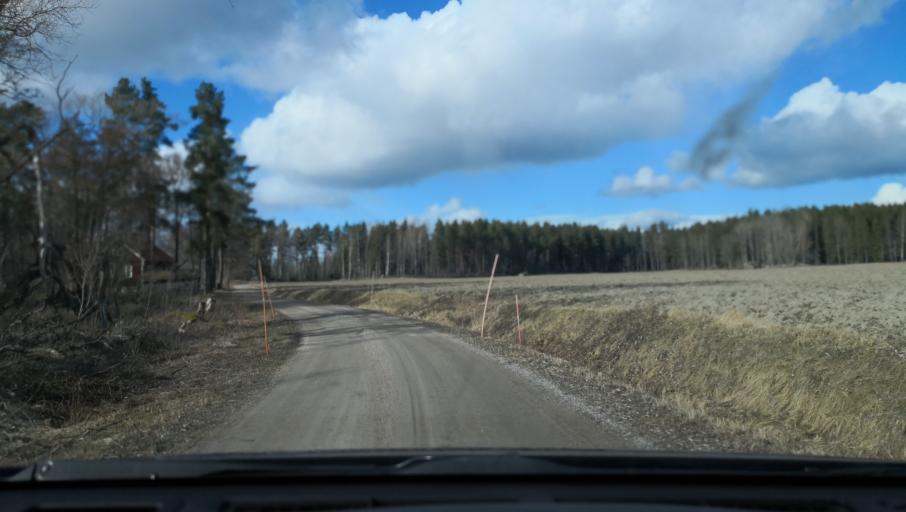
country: SE
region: OErebro
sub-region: Lindesbergs Kommun
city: Fellingsbro
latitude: 59.4253
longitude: 15.6876
